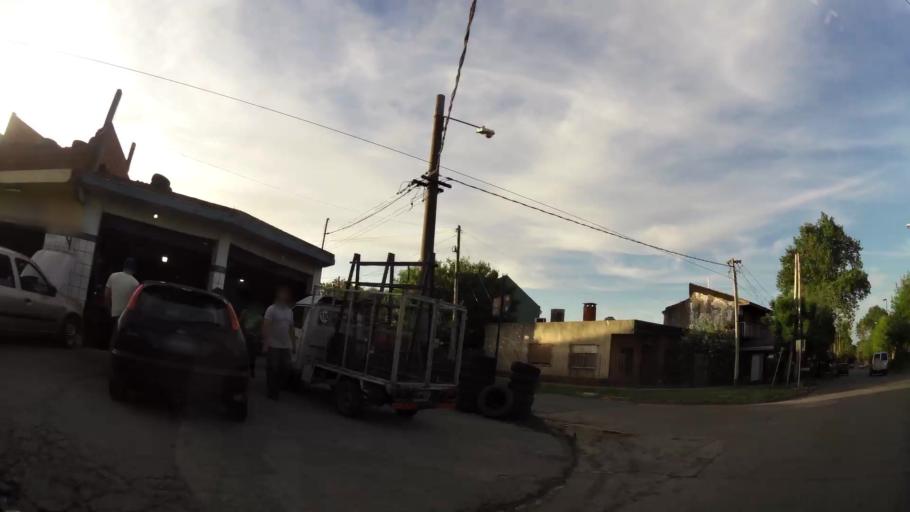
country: AR
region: Buenos Aires
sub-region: Partido de Quilmes
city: Quilmes
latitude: -34.7792
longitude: -58.1978
